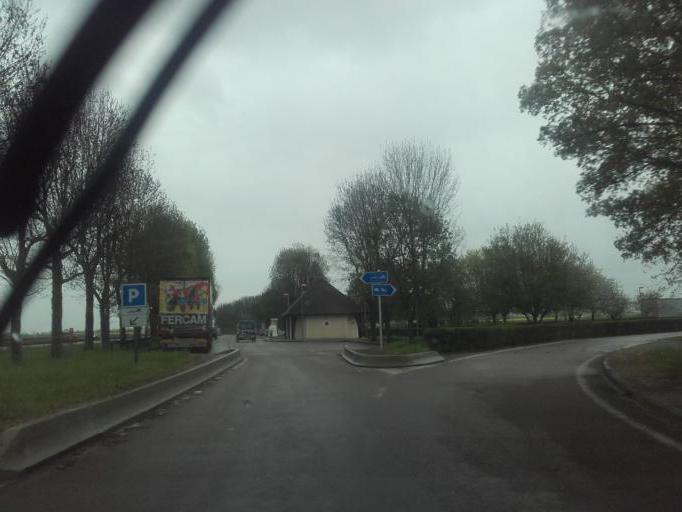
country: FR
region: Bourgogne
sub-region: Departement de la Cote-d'Or
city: Semur-en-Auxois
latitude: 47.4858
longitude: 4.1580
